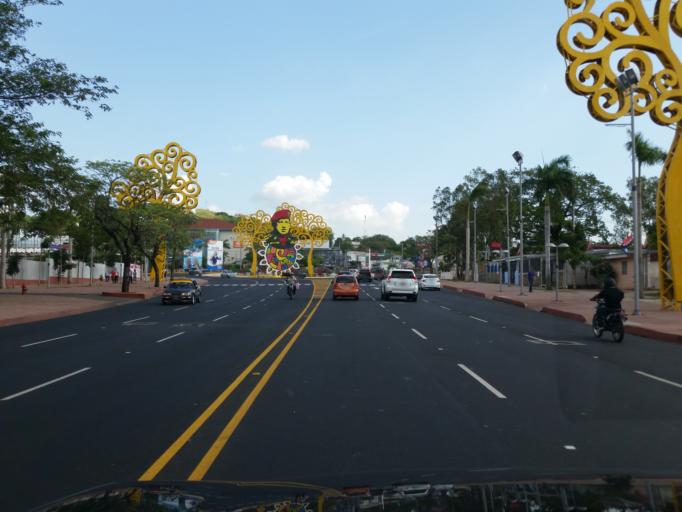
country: NI
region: Managua
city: Managua
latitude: 12.1476
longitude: -86.2746
